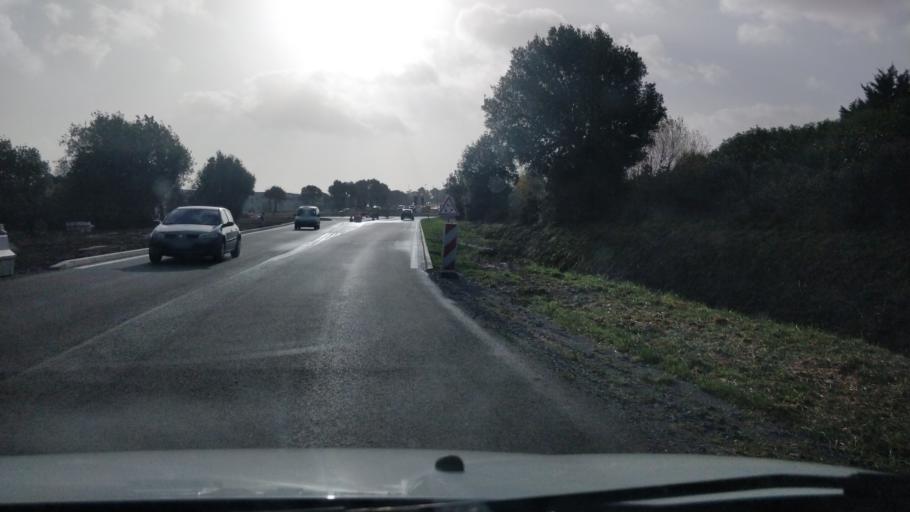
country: FR
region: Pays de la Loire
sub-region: Departement de la Loire-Atlantique
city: Guerande
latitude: 47.3307
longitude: -2.4169
